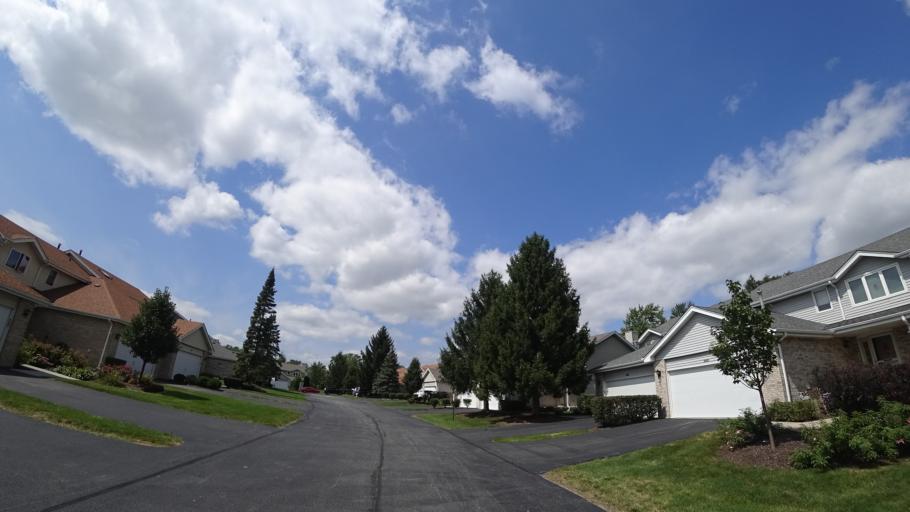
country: US
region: Illinois
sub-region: Cook County
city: Orland Hills
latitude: 41.5718
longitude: -87.8476
